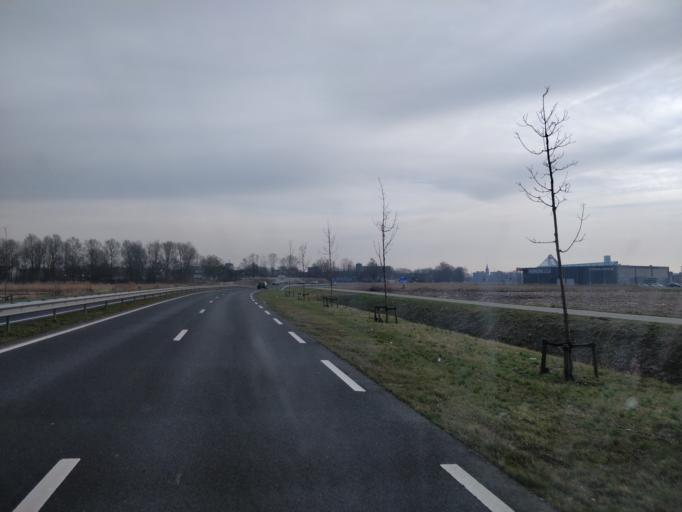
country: NL
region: Friesland
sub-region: Menameradiel
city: Marsum
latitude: 53.2071
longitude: 5.7570
